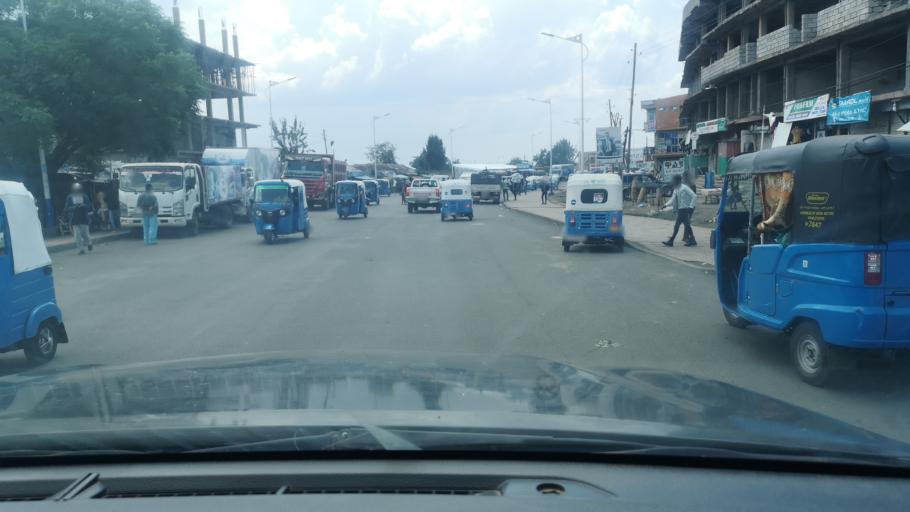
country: ET
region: Oromiya
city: Waliso
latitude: 8.2834
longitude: 37.7797
